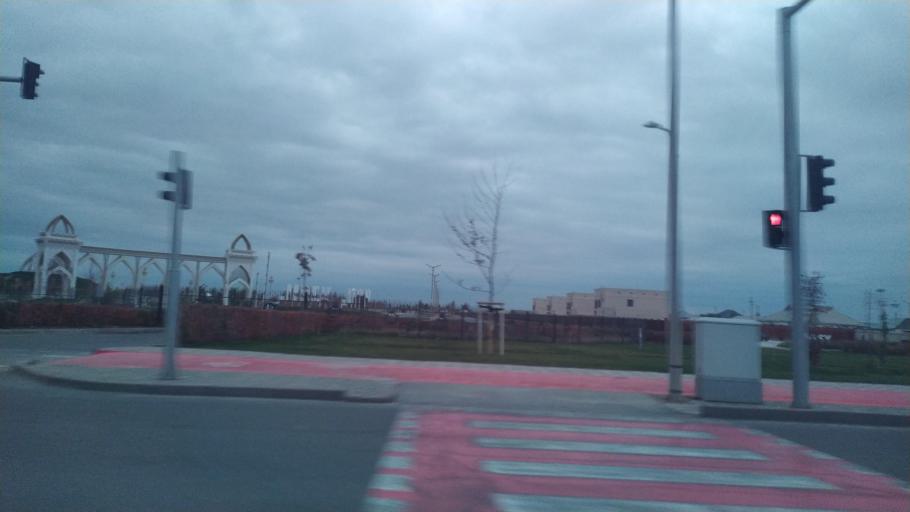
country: KZ
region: Ongtustik Qazaqstan
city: Turkestan
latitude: 43.2768
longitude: 68.3310
